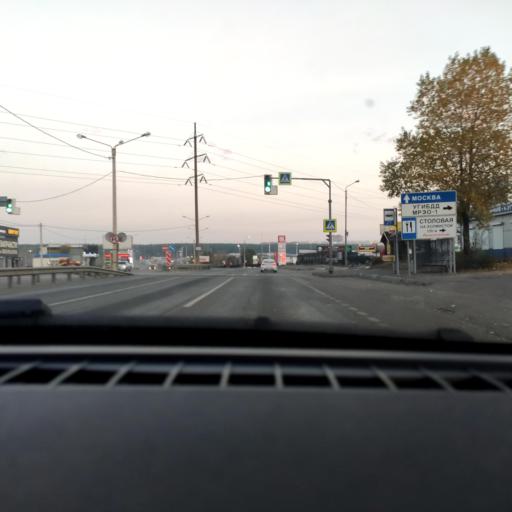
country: RU
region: Voronezj
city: Voronezh
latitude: 51.6662
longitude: 39.1273
